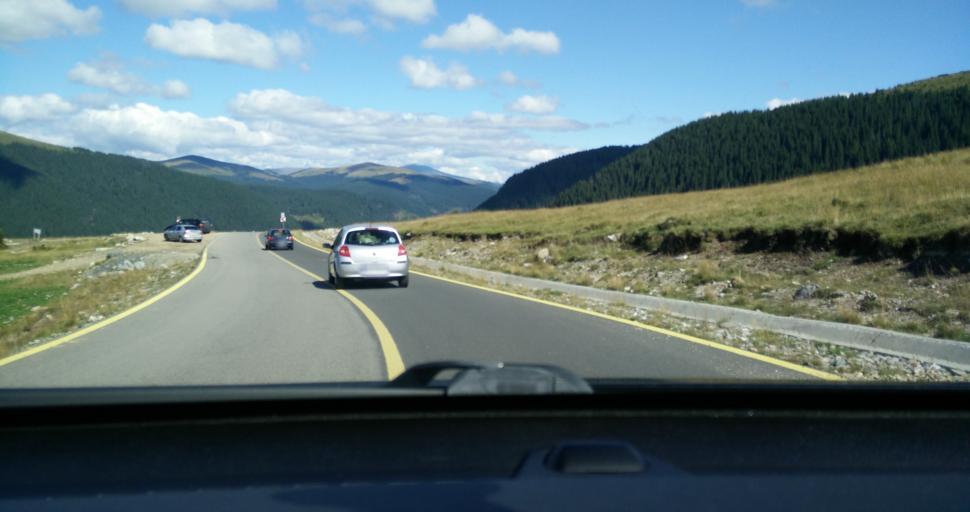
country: RO
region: Gorj
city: Novaci-Straini
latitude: 45.3846
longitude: 23.6429
